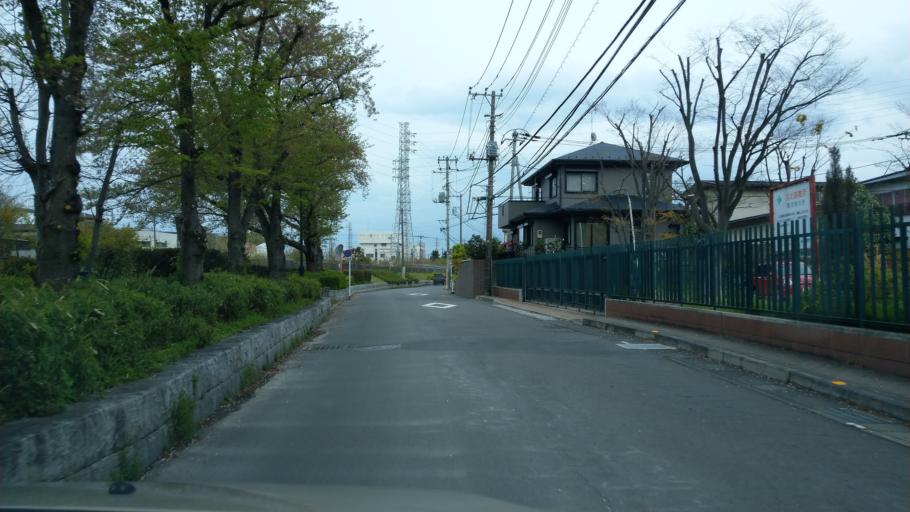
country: JP
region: Saitama
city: Ageoshimo
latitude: 35.9381
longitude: 139.5973
